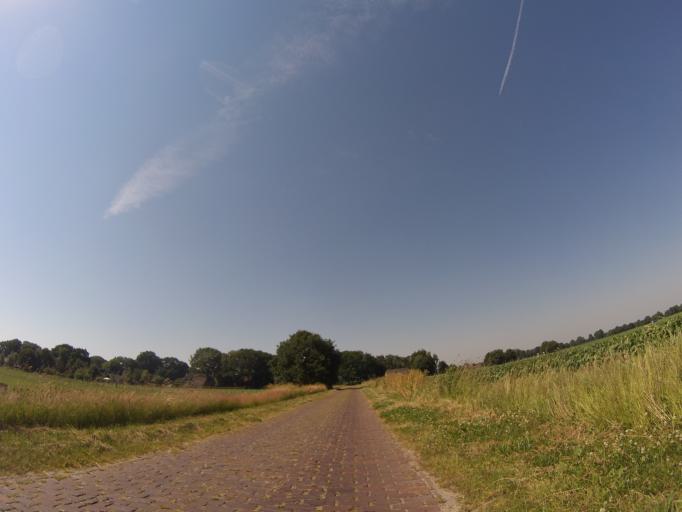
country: NL
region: Drenthe
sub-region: Gemeente Coevorden
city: Sleen
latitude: 52.7811
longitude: 6.7427
